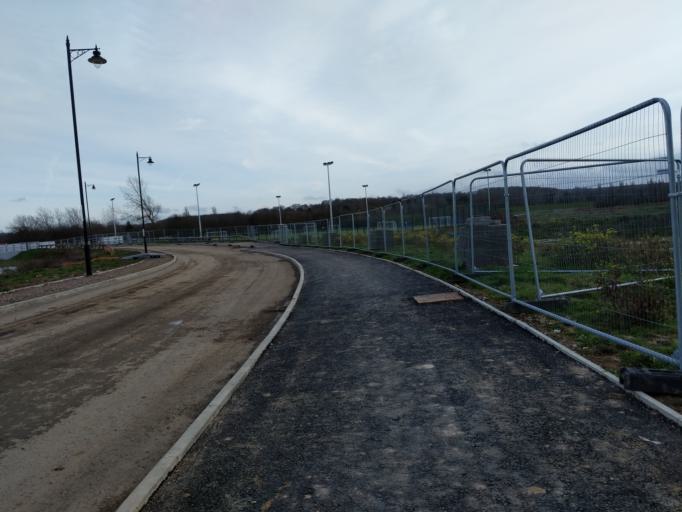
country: GB
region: England
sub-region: Kent
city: Herne Bay
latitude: 51.3568
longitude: 1.1180
